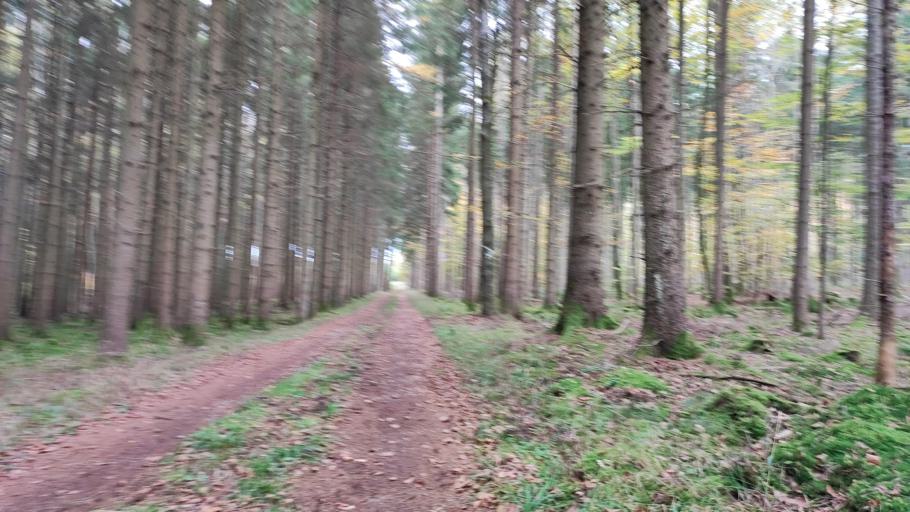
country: DE
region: Bavaria
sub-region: Swabia
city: Munsterhausen
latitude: 48.3237
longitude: 10.4967
